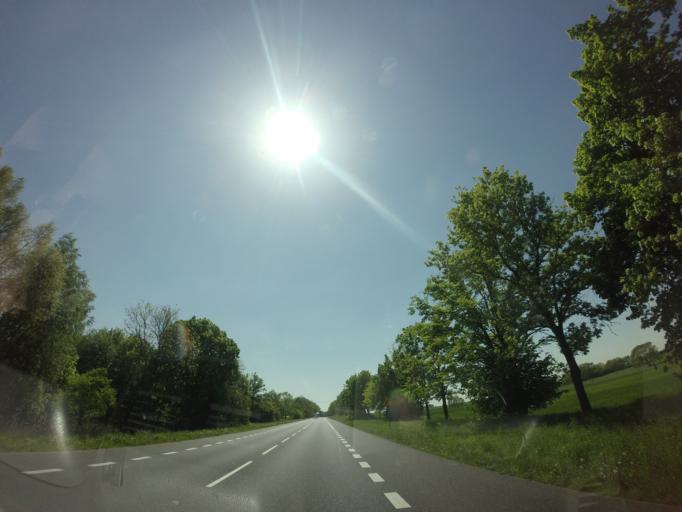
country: PL
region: West Pomeranian Voivodeship
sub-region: Powiat pyrzycki
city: Lipiany
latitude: 52.9823
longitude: 14.9777
